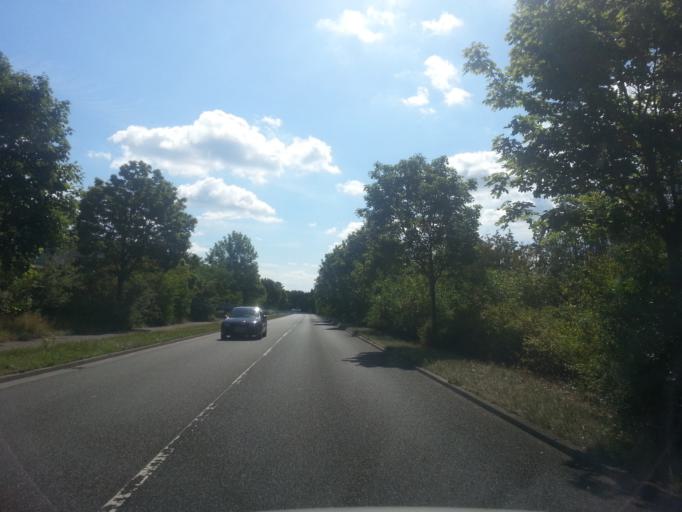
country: DE
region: Hesse
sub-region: Regierungsbezirk Darmstadt
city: Eppertshausen
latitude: 49.9689
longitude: 8.8208
